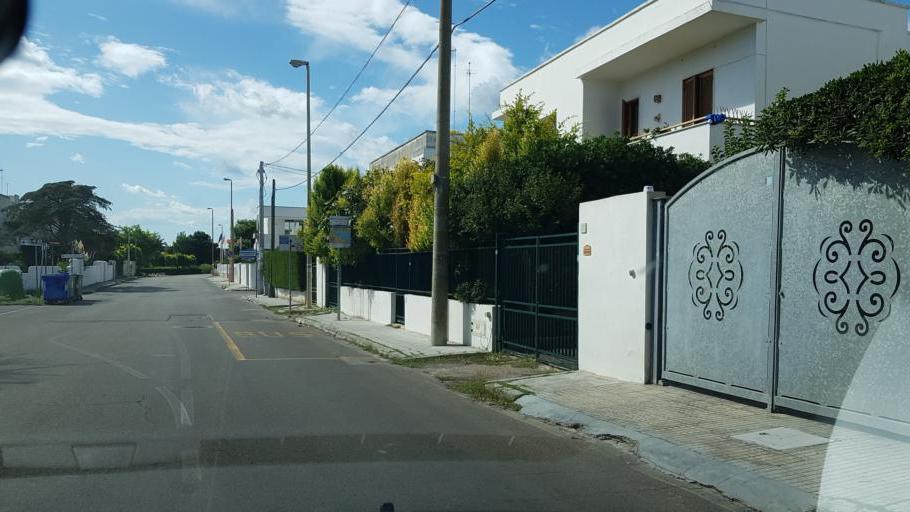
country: IT
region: Apulia
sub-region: Provincia di Lecce
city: Borgagne
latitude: 40.2711
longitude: 18.4287
